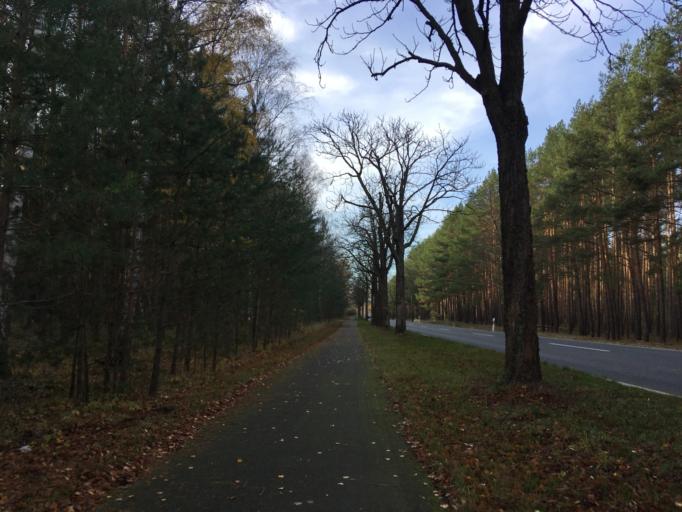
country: DE
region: Brandenburg
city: Halbe
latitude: 52.1064
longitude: 13.7132
